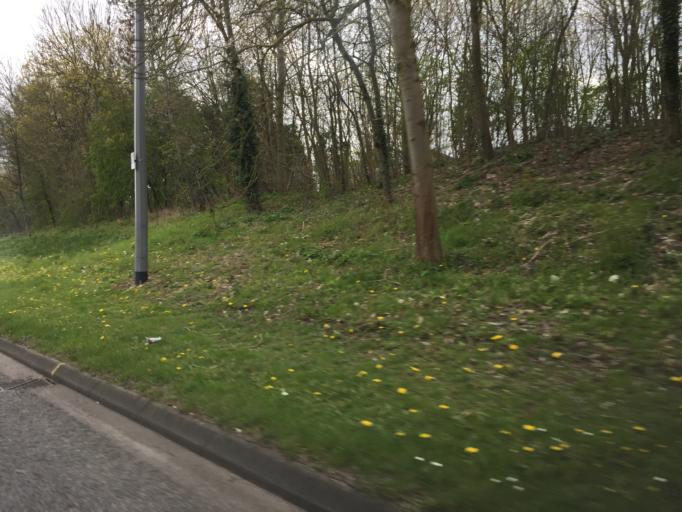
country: GB
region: England
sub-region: Milton Keynes
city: Milton Keynes
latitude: 52.0478
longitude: -0.7657
